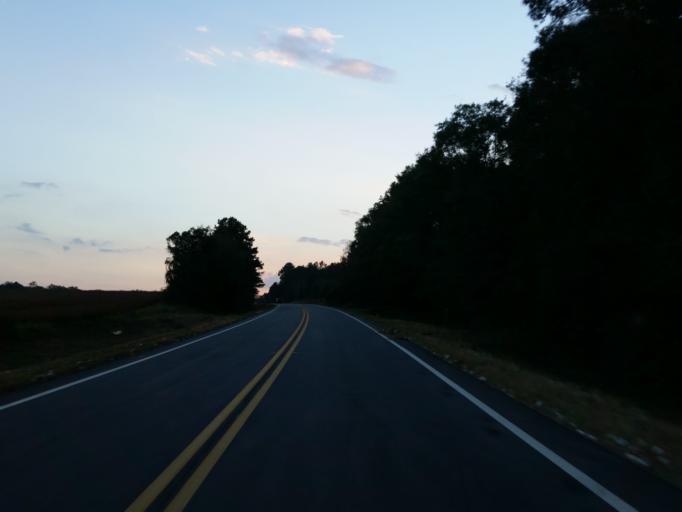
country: US
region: Georgia
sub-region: Pulaski County
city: Hawkinsville
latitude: 32.2162
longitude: -83.5286
